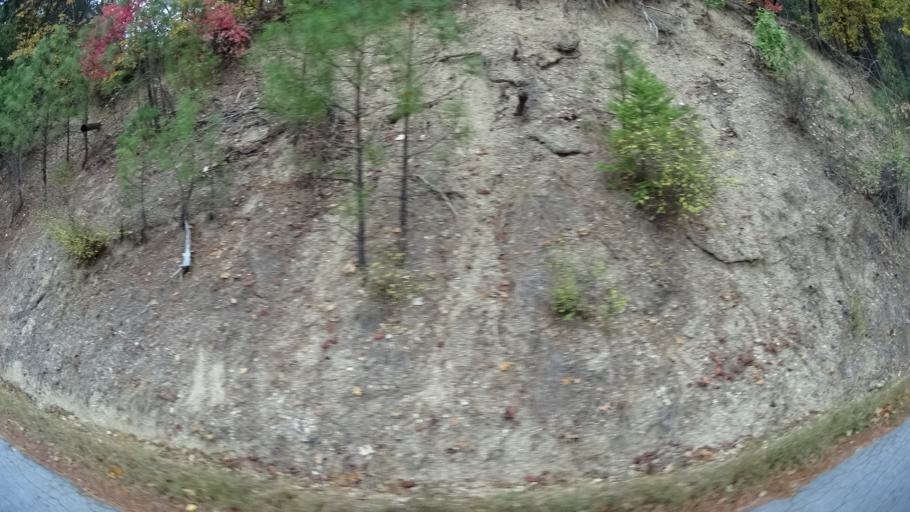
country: US
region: California
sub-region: Siskiyou County
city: Happy Camp
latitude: 41.8285
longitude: -123.1808
